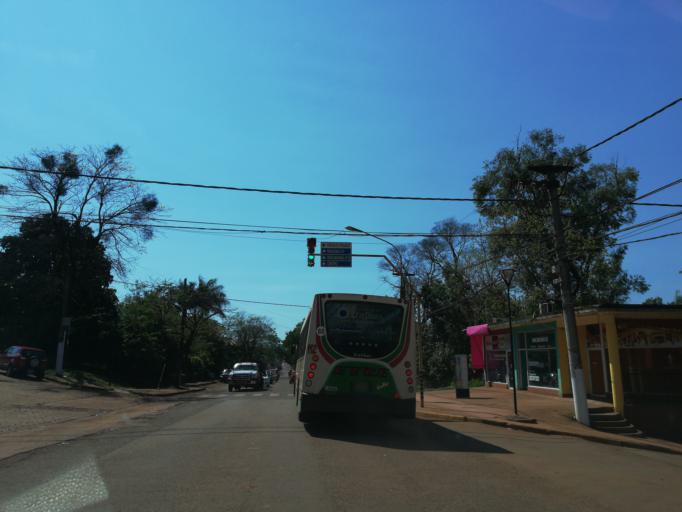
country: AR
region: Misiones
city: Puerto Eldorado
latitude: -26.4071
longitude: -54.6658
